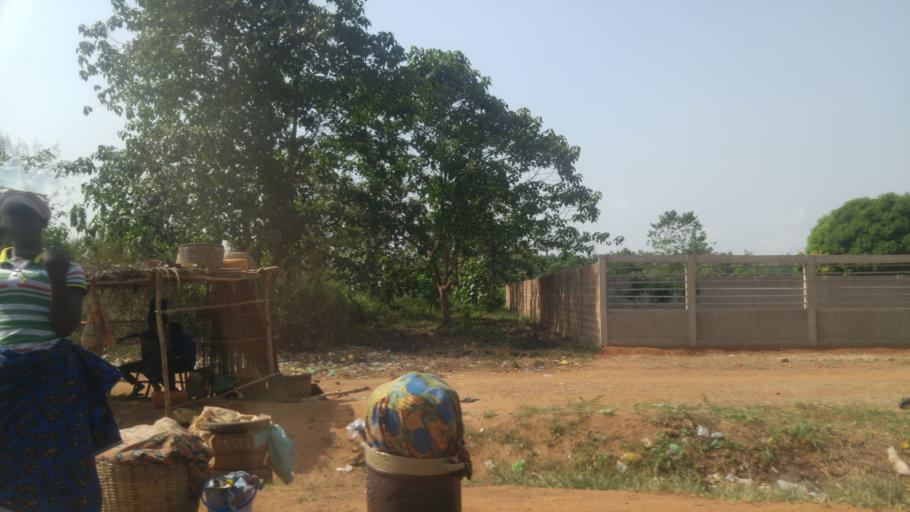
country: BJ
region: Zou
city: Bohicon
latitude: 7.0216
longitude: 2.1786
